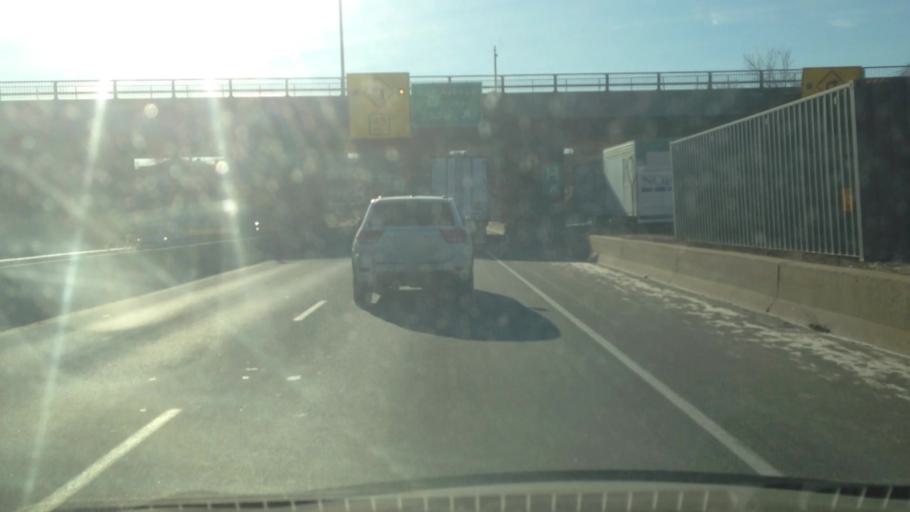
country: CA
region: Quebec
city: Cote-Saint-Luc
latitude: 45.4500
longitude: -73.6972
